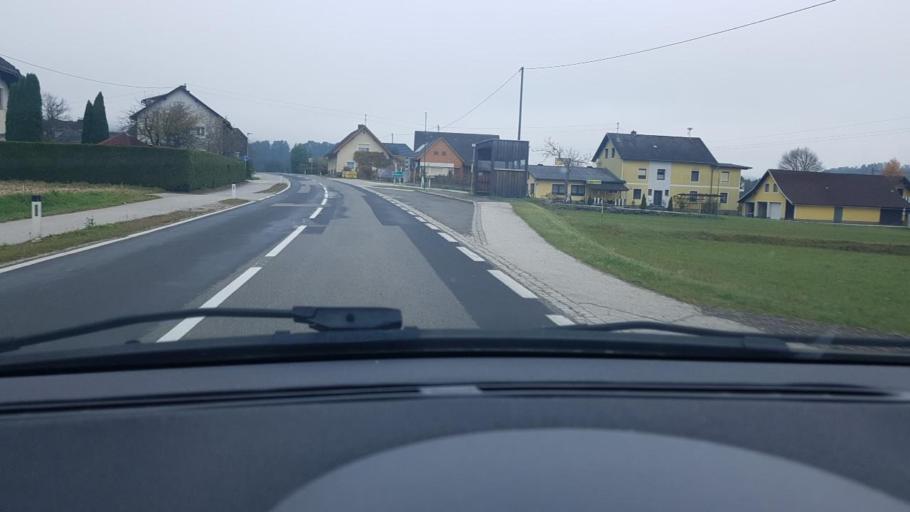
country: AT
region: Carinthia
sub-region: Politischer Bezirk Volkermarkt
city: Neuhaus
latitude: 46.6464
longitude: 14.9059
